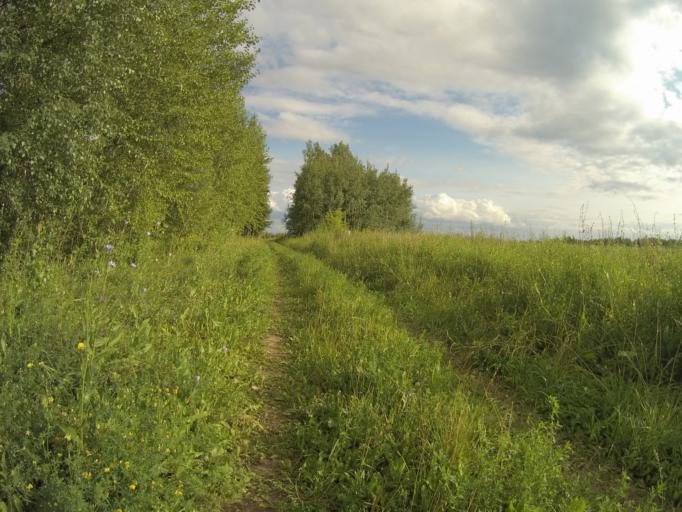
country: RU
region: Vladimir
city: Vladimir
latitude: 56.1844
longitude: 40.4477
